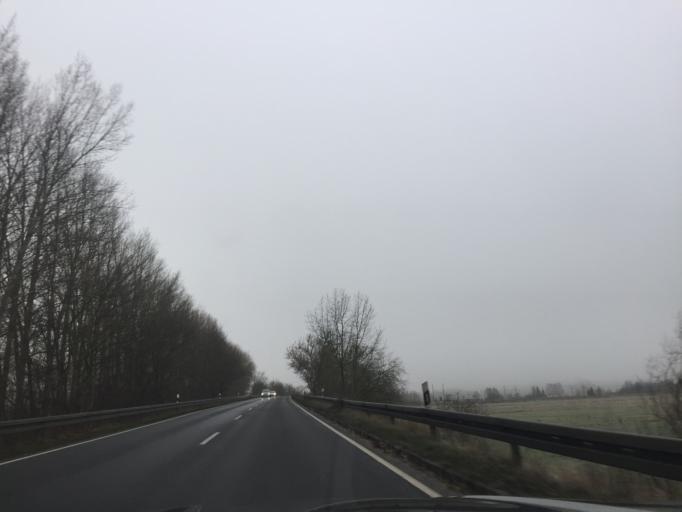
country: DE
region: Brandenburg
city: Velten
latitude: 52.6445
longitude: 13.1474
